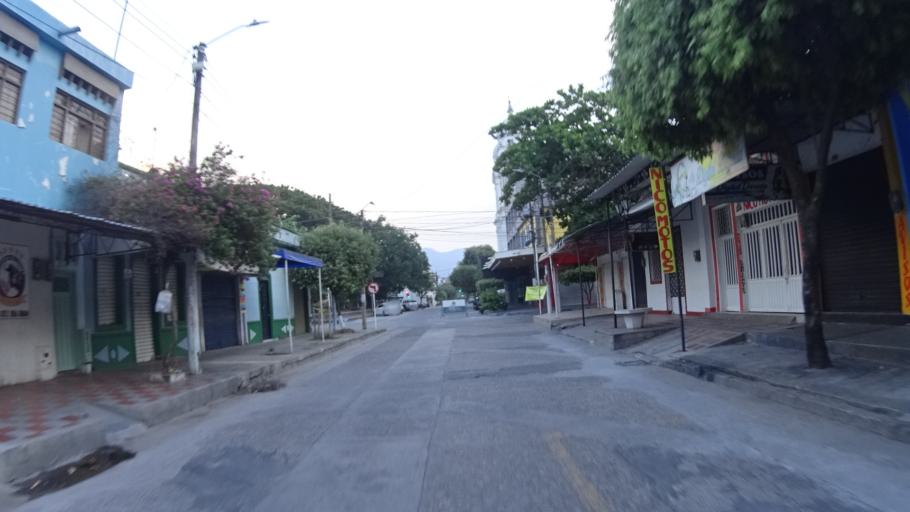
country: CO
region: Caldas
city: La Dorada
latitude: 5.4550
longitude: -74.6640
